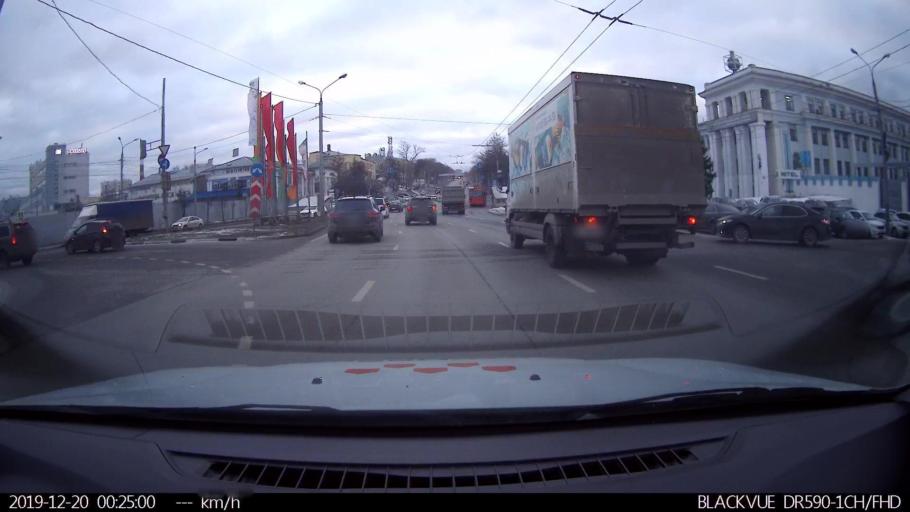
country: RU
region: Vladimir
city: Yur'yev-Pol'skiy
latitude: 56.6603
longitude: 39.5370
